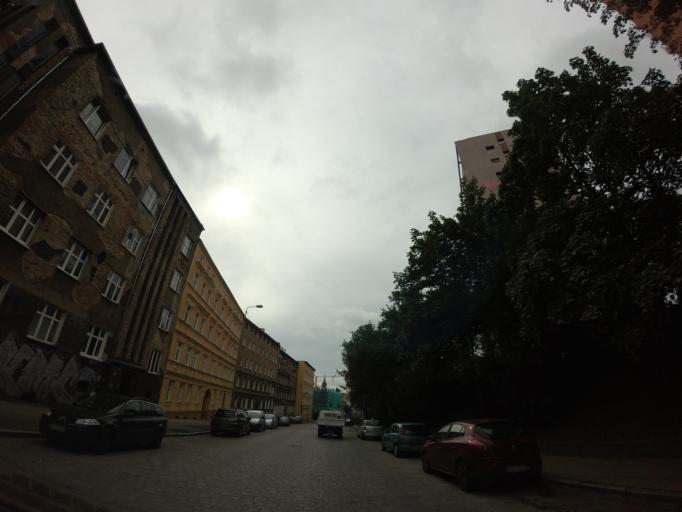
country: PL
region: West Pomeranian Voivodeship
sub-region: Szczecin
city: Szczecin
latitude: 53.4474
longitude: 14.5447
